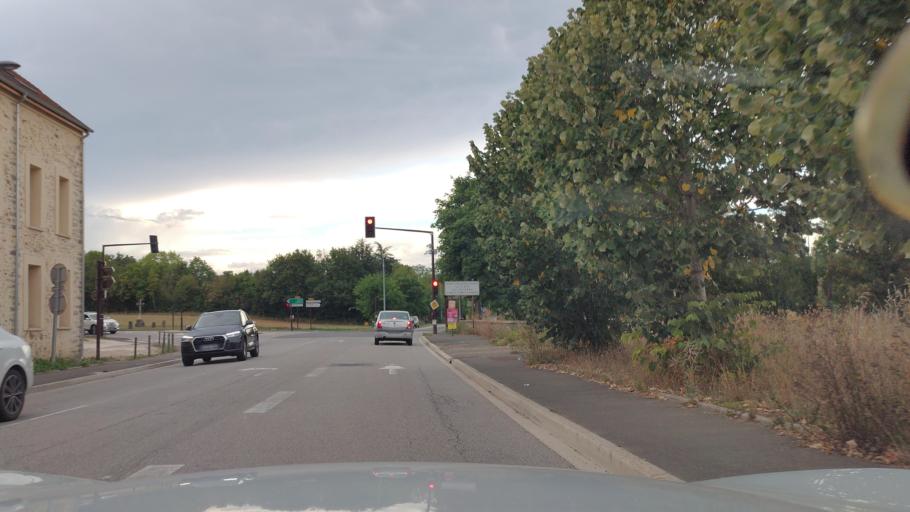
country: FR
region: Ile-de-France
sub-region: Departement de Seine-et-Marne
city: Guignes
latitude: 48.6377
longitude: 2.7944
